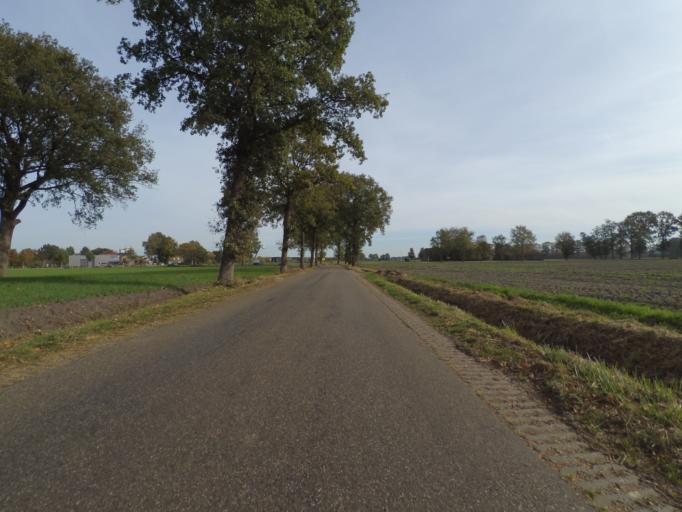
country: NL
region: Overijssel
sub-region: Gemeente Raalte
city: Raalte
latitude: 52.3251
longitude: 6.2810
